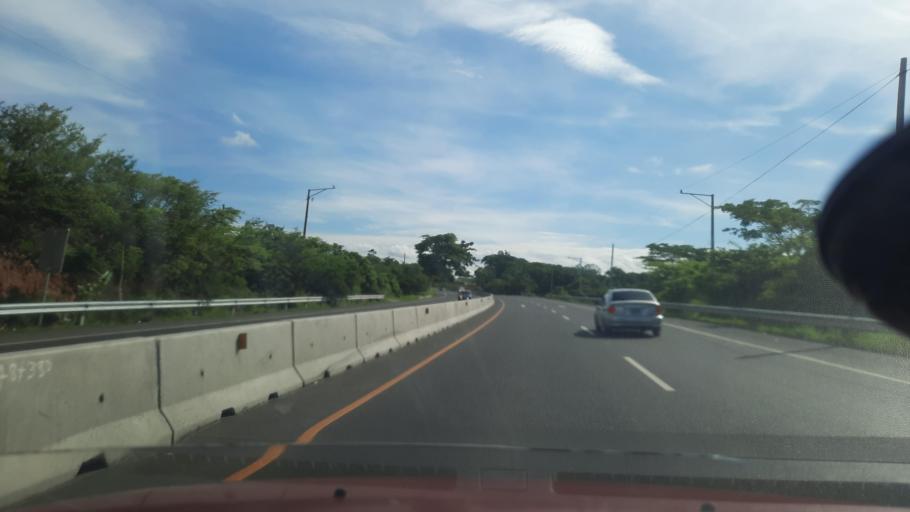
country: SV
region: La Paz
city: El Rosario
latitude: 13.4780
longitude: -89.0000
